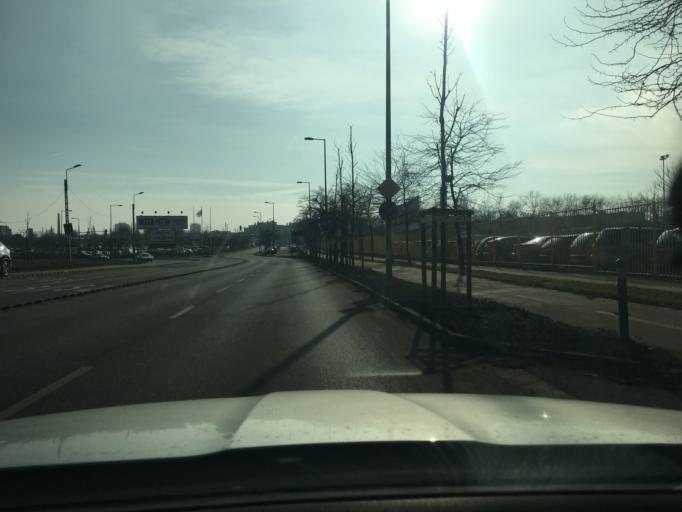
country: HU
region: Budapest
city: Budapest X. keruelet
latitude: 47.4958
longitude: 19.1380
